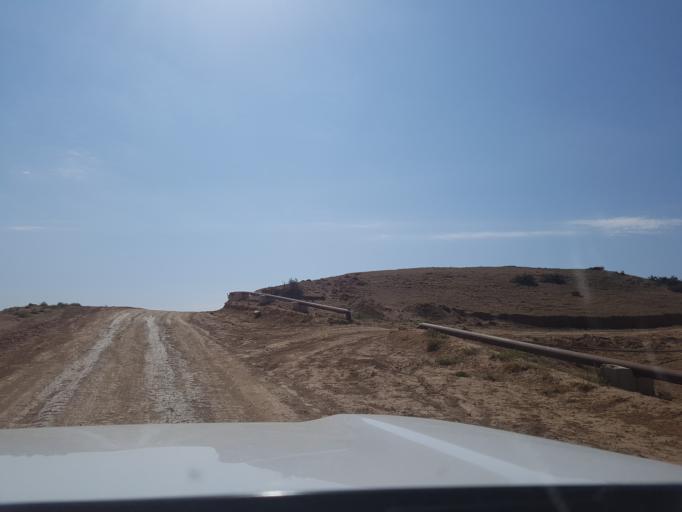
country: TM
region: Ahal
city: Baharly
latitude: 38.3280
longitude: 56.9525
